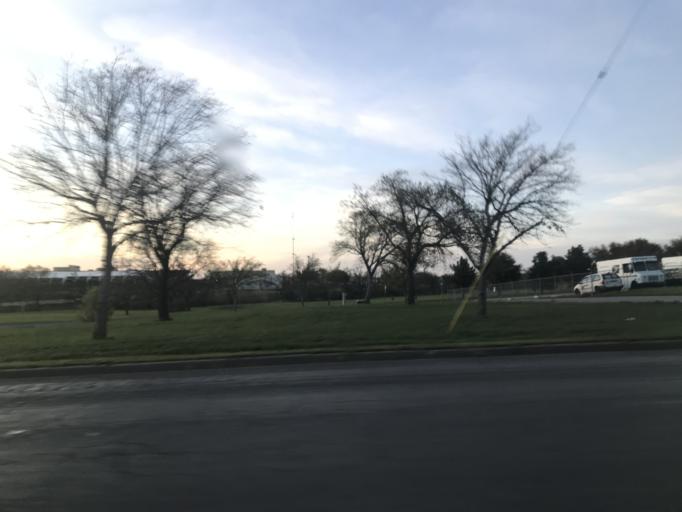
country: US
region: Texas
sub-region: Tom Green County
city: San Angelo
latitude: 31.4608
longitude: -100.4472
